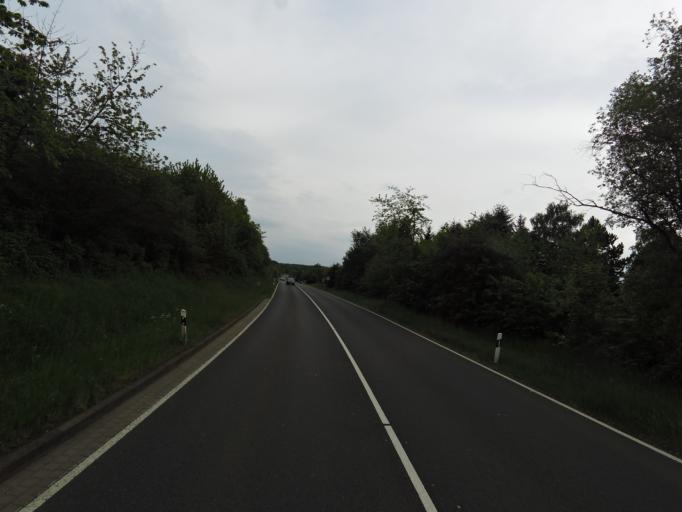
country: DE
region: Rheinland-Pfalz
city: Waldesch
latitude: 50.2845
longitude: 7.5474
